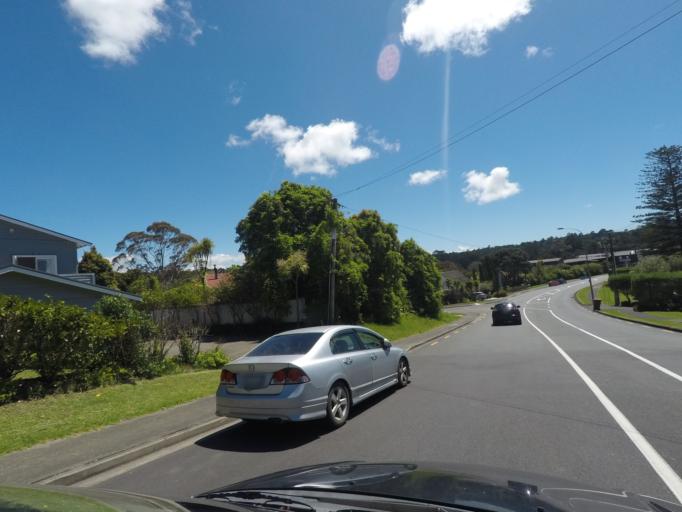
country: NZ
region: Auckland
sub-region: Auckland
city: Rothesay Bay
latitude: -36.7260
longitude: 174.6881
